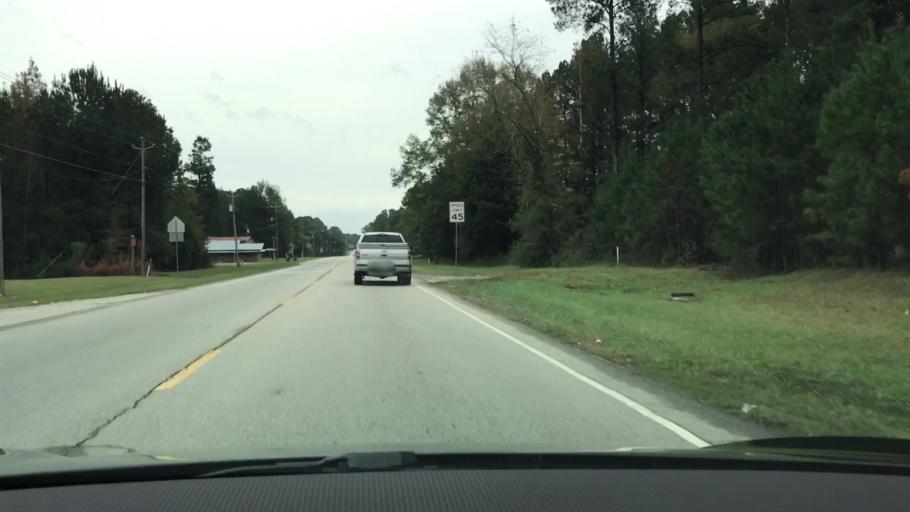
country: US
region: Georgia
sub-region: Warren County
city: West Warrenton
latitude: 33.4160
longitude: -82.6774
